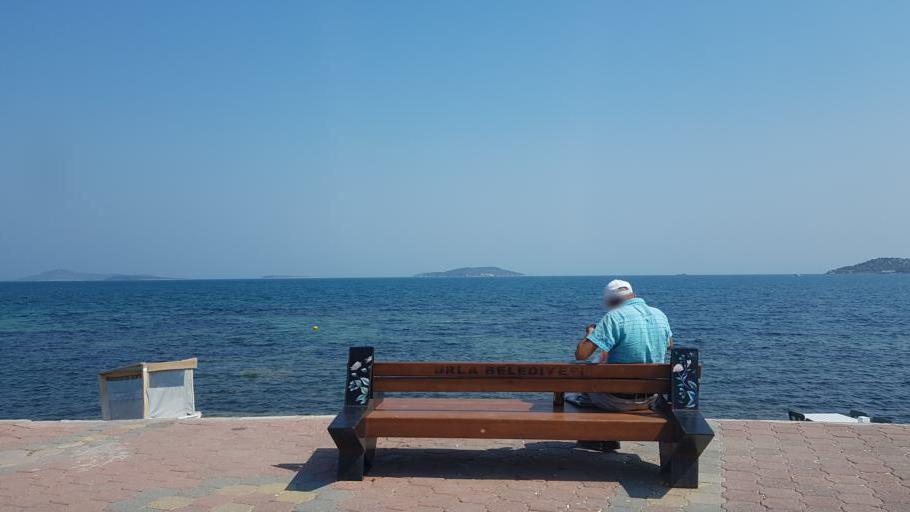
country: TR
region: Izmir
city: Urla
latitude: 38.3662
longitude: 26.7673
